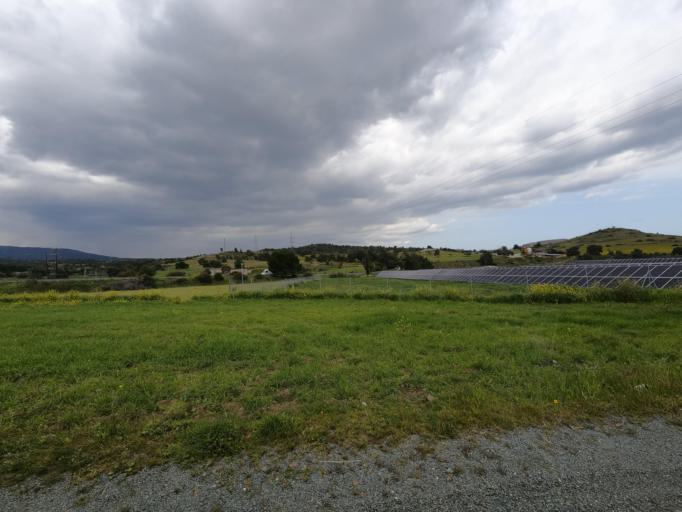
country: CY
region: Lefkosia
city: Lefka
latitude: 35.0714
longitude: 32.9261
